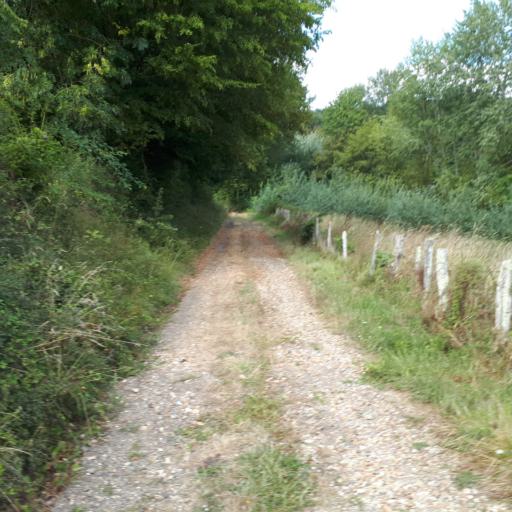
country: FR
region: Centre
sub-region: Departement du Loir-et-Cher
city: Villiers-sur-Loir
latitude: 47.8263
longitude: 0.9893
